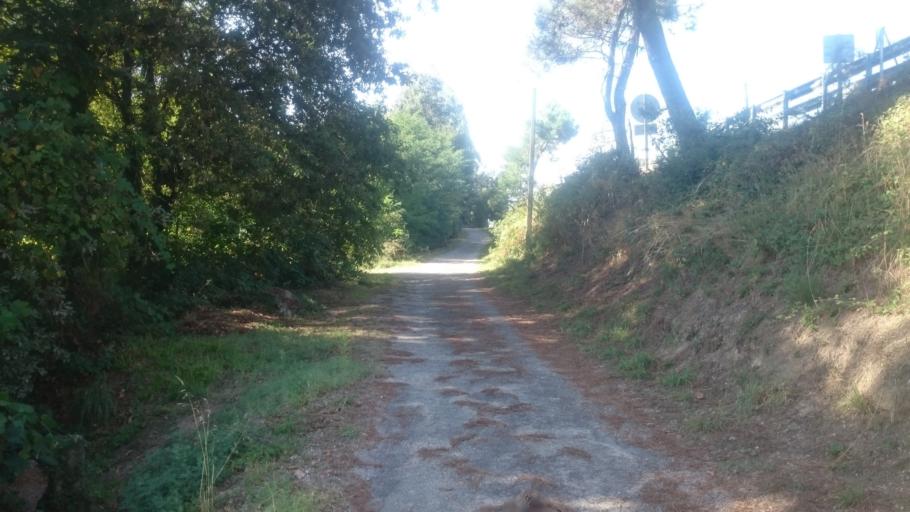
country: ES
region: Galicia
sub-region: Provincia de Pontevedra
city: Porrino
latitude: 42.1633
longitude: -8.6120
